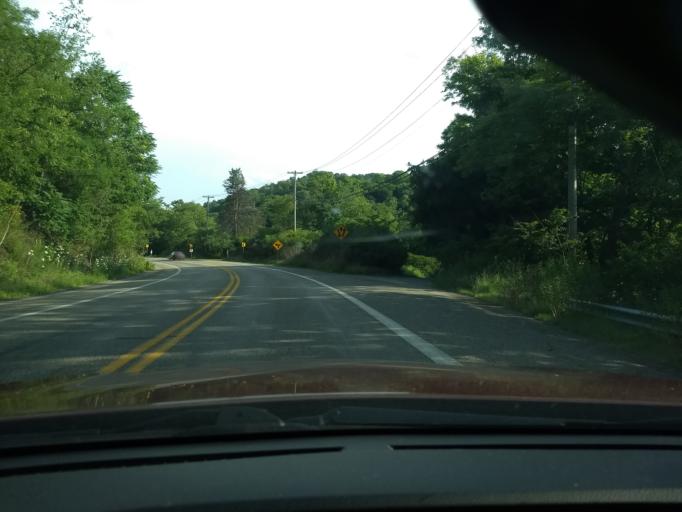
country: US
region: Pennsylvania
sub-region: Allegheny County
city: Tarentum
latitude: 40.6185
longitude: -79.7631
